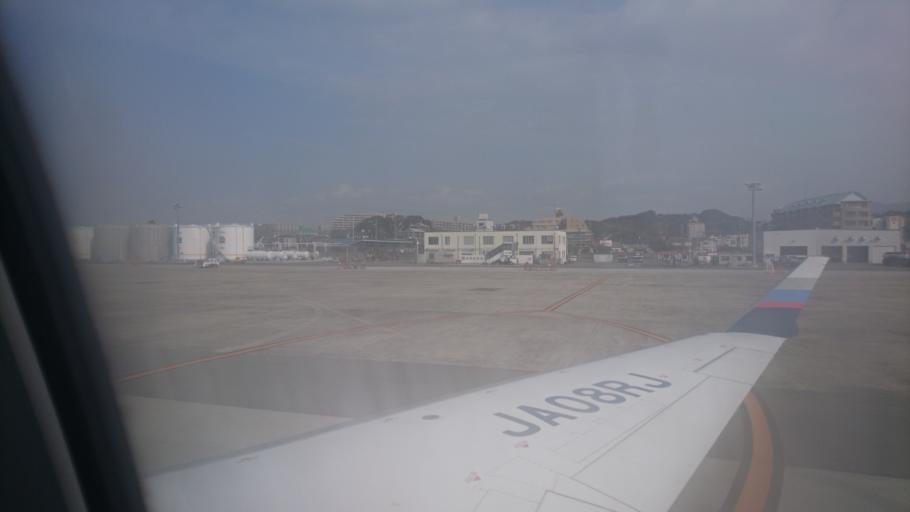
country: JP
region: Fukuoka
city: Fukuoka-shi
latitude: 33.5884
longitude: 130.4513
